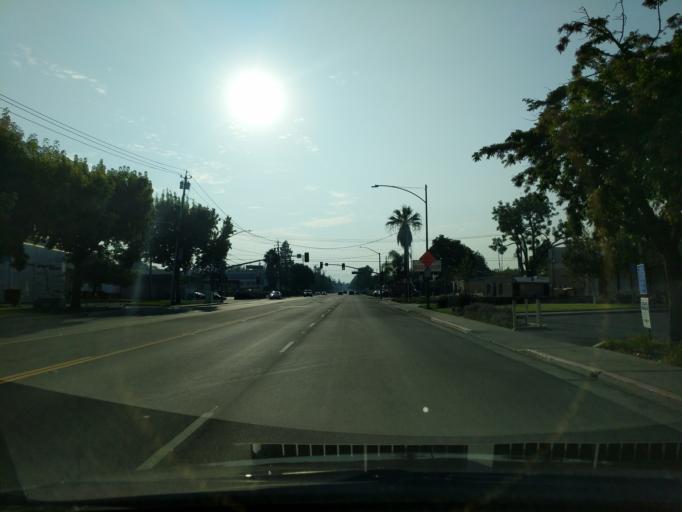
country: US
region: California
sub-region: Santa Clara County
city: Mountain View
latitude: 37.4143
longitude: -122.0883
